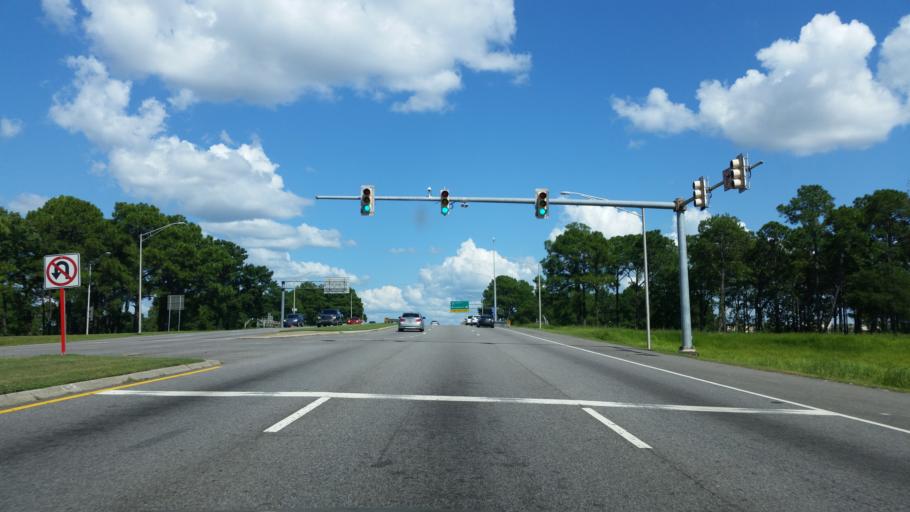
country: US
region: Alabama
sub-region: Mobile County
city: Prichard
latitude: 30.6761
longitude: -88.1292
